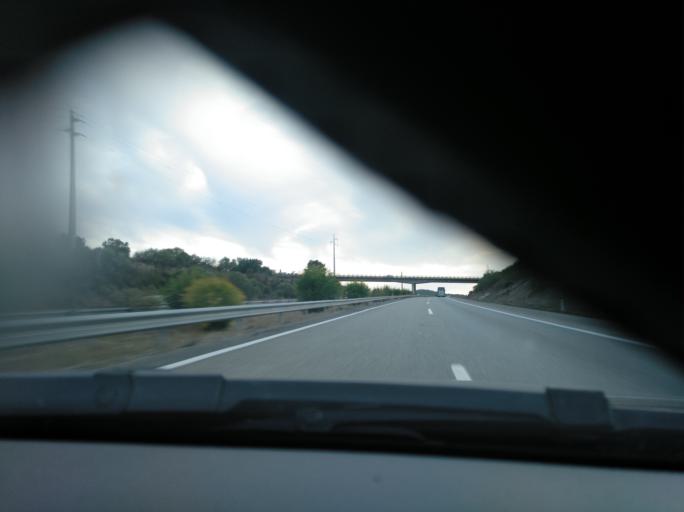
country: PT
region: Evora
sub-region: Montemor-O-Novo
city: Montemor-o-Novo
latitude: 38.6495
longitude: -8.2550
